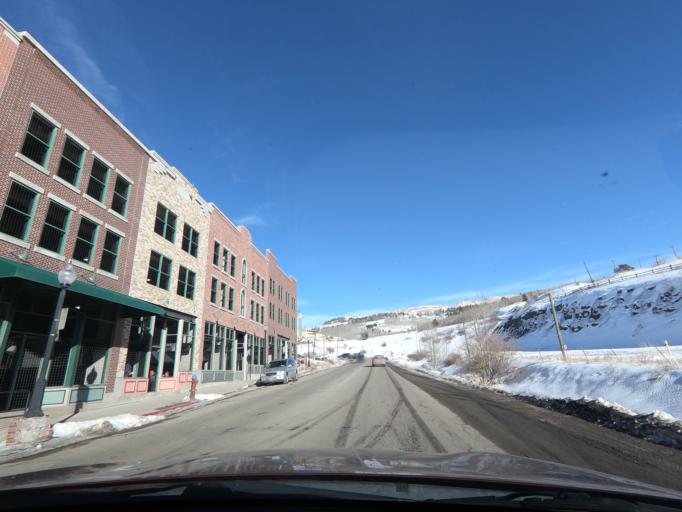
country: US
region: Colorado
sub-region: Teller County
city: Cripple Creek
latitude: 38.7459
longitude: -105.1742
